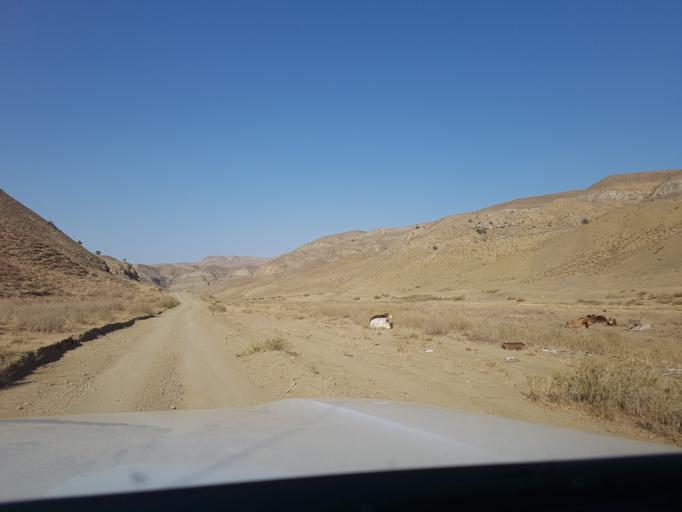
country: TM
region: Balkan
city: Magtymguly
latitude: 38.3011
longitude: 56.7658
